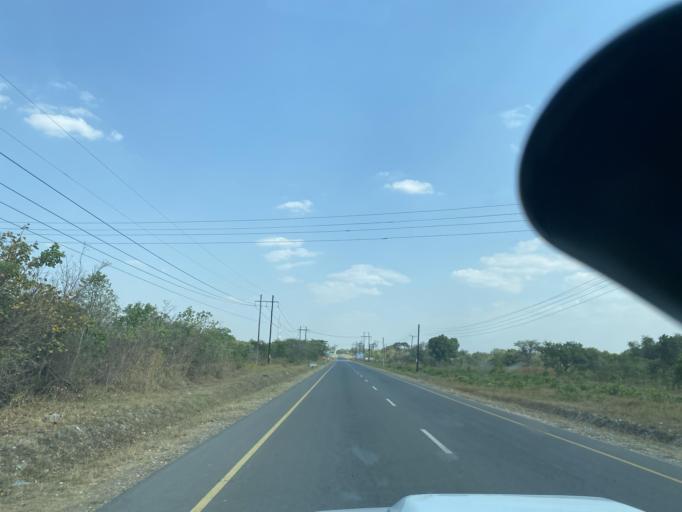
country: ZM
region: Lusaka
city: Lusaka
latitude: -15.3337
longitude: 28.0722
